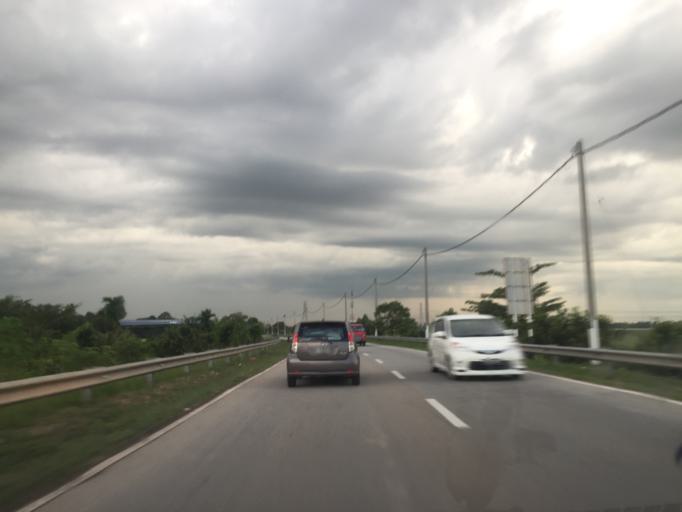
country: MY
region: Penang
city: Tasek Glugor
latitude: 5.5607
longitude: 100.5013
